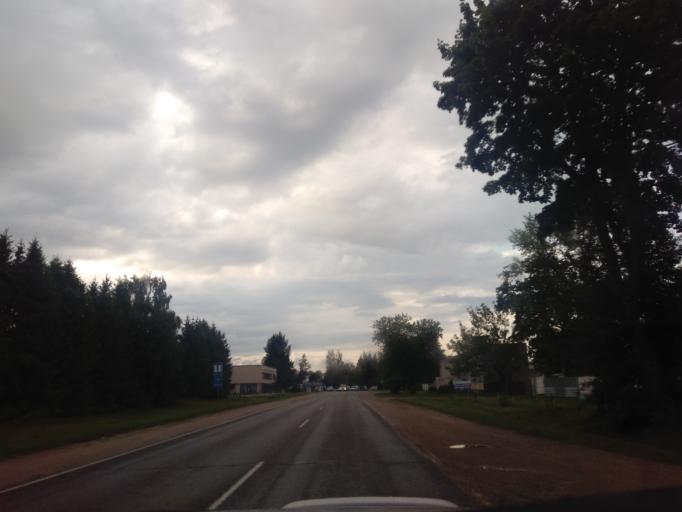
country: BY
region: Minsk
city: Enyerhyetykaw
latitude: 53.5833
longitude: 27.0538
